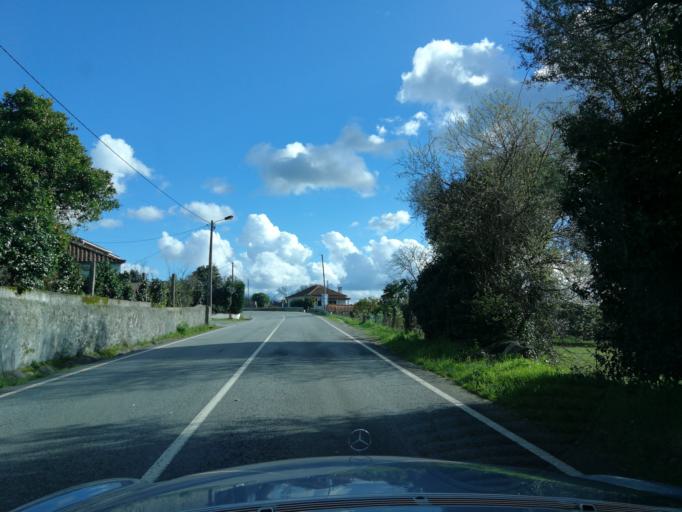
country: PT
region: Braga
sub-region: Vila Verde
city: Prado
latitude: 41.6689
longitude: -8.5233
